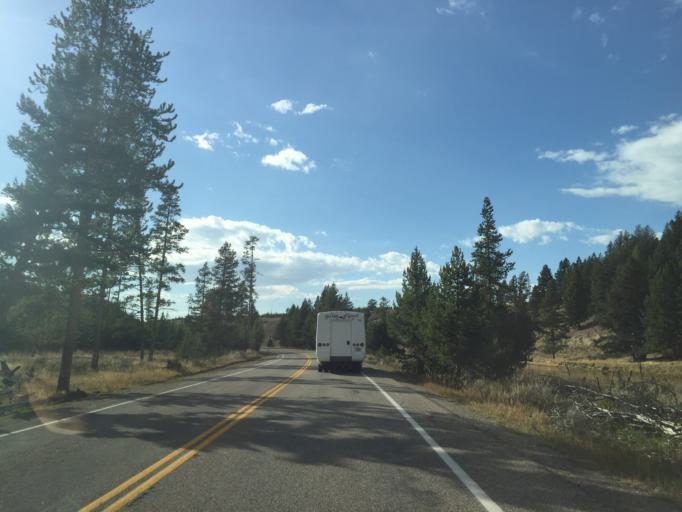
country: US
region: Montana
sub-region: Gallatin County
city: West Yellowstone
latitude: 44.6690
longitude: -110.9754
